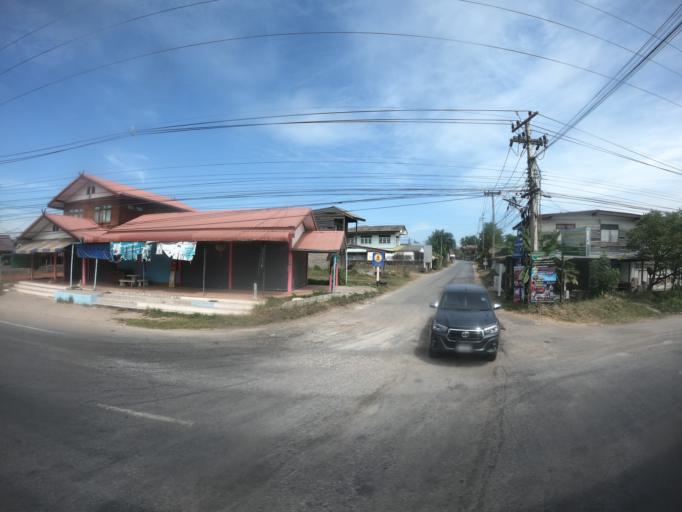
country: TH
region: Maha Sarakham
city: Chiang Yuen
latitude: 16.4459
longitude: 103.0311
